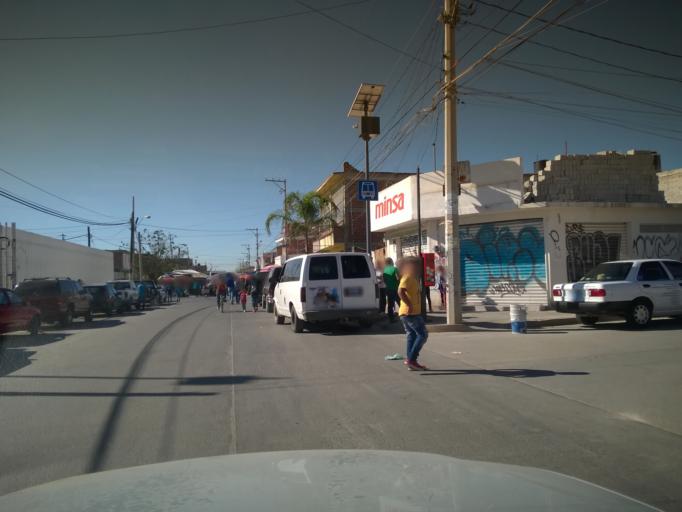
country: MX
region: Guanajuato
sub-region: Leon
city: San Jose de Duran (Los Troncoso)
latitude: 21.0704
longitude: -101.6350
